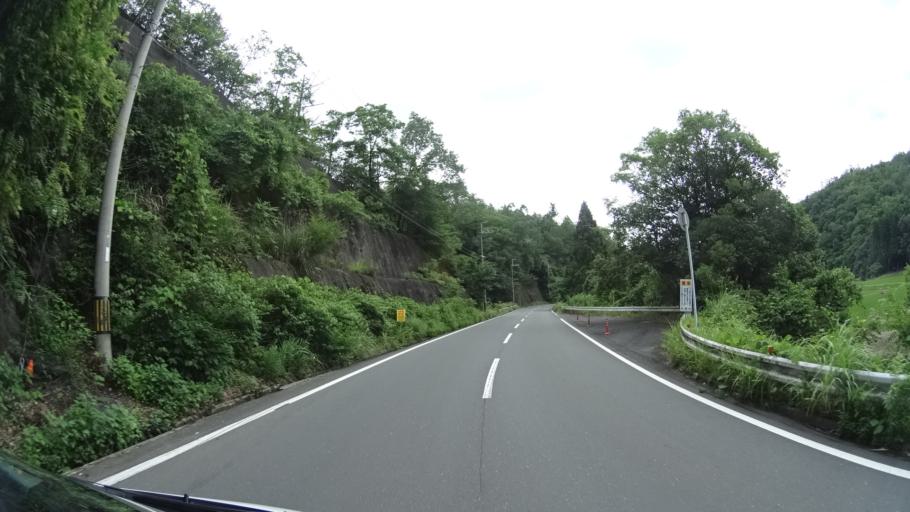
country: JP
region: Kyoto
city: Kameoka
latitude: 35.0814
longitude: 135.4110
